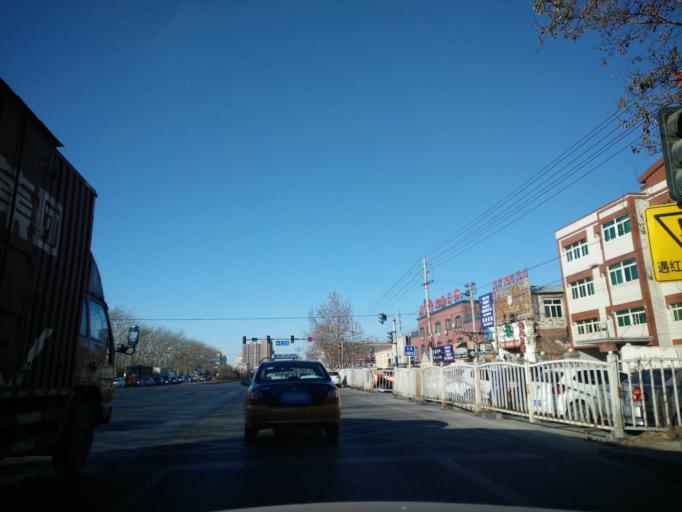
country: CN
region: Beijing
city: Xingfeng
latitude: 39.7207
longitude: 116.3539
